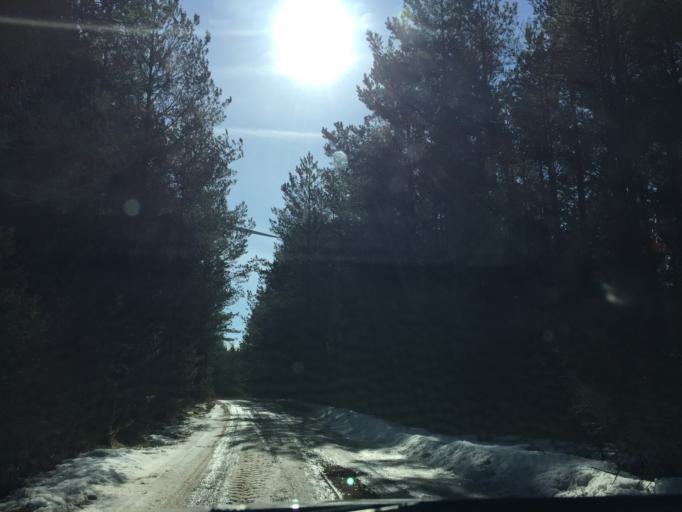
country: EE
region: Laeaene
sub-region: Haapsalu linn
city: Haapsalu
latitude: 58.6388
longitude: 23.5183
